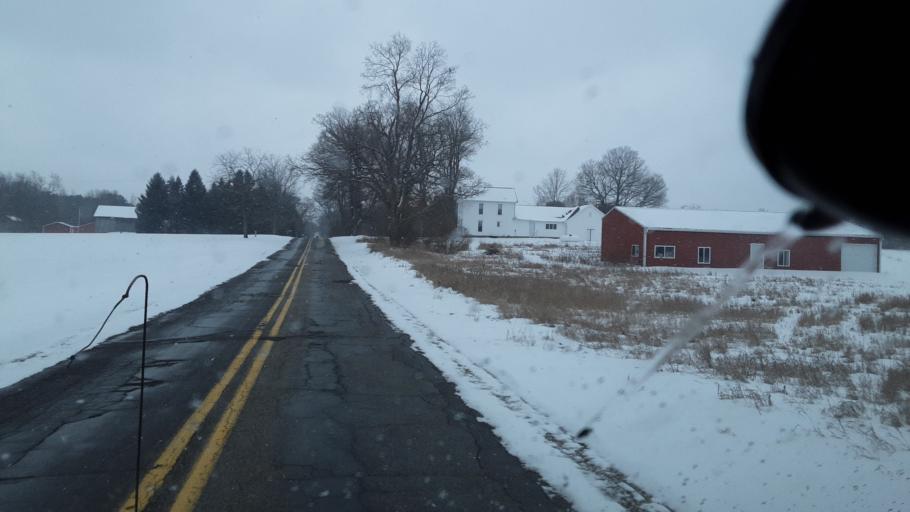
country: US
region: Michigan
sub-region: Ingham County
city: Leslie
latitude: 42.4857
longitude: -84.3942
